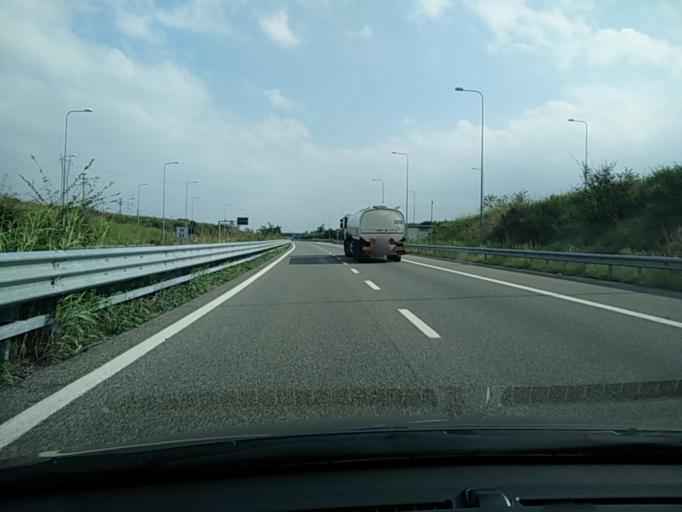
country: IT
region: Lombardy
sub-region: Citta metropolitana di Milano
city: Casate
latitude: 45.5016
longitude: 8.8341
